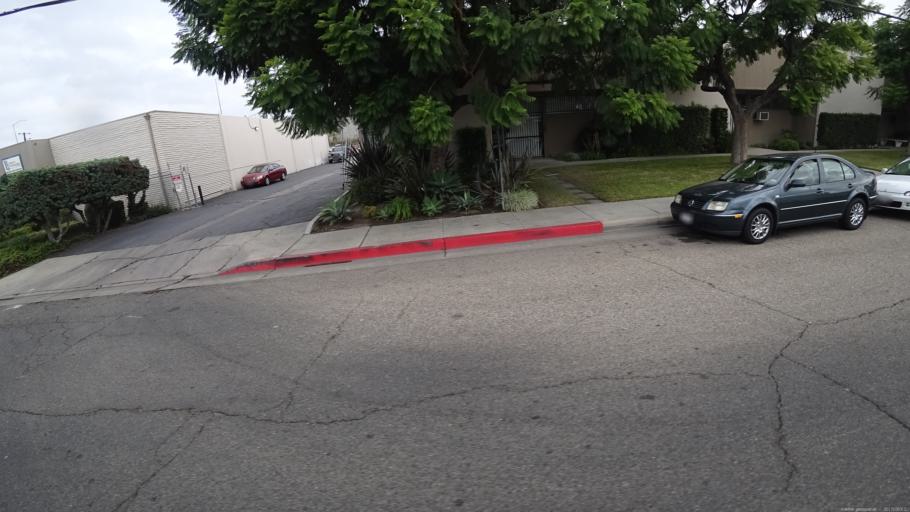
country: US
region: California
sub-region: Orange County
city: Garden Grove
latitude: 33.7653
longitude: -117.9241
